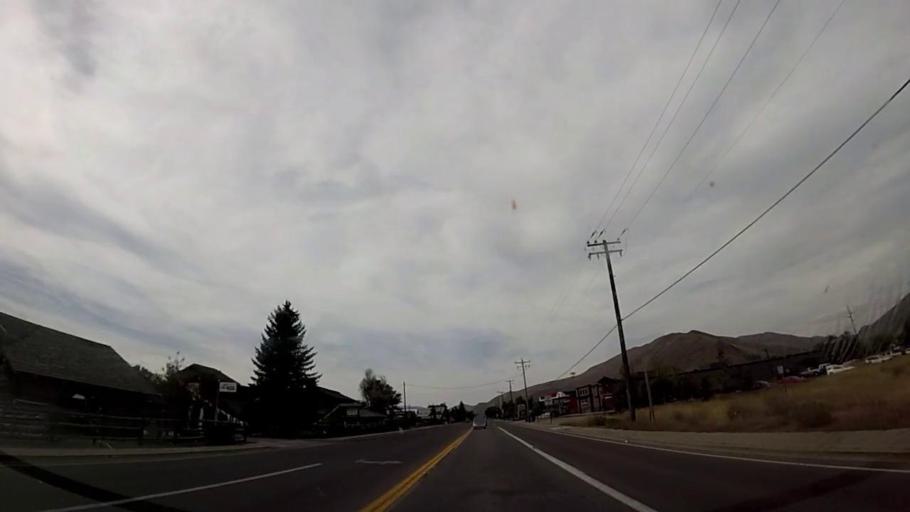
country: US
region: Idaho
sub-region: Blaine County
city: Bellevue
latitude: 43.4560
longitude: -114.2570
